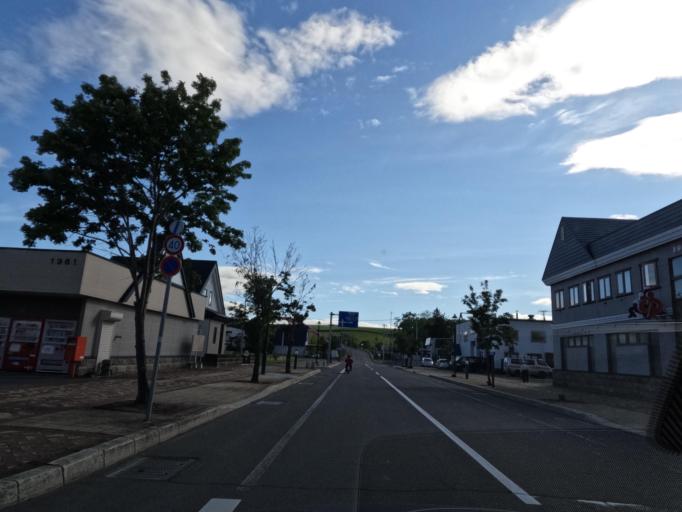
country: JP
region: Hokkaido
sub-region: Asahikawa-shi
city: Asahikawa
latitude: 43.5879
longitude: 142.4585
